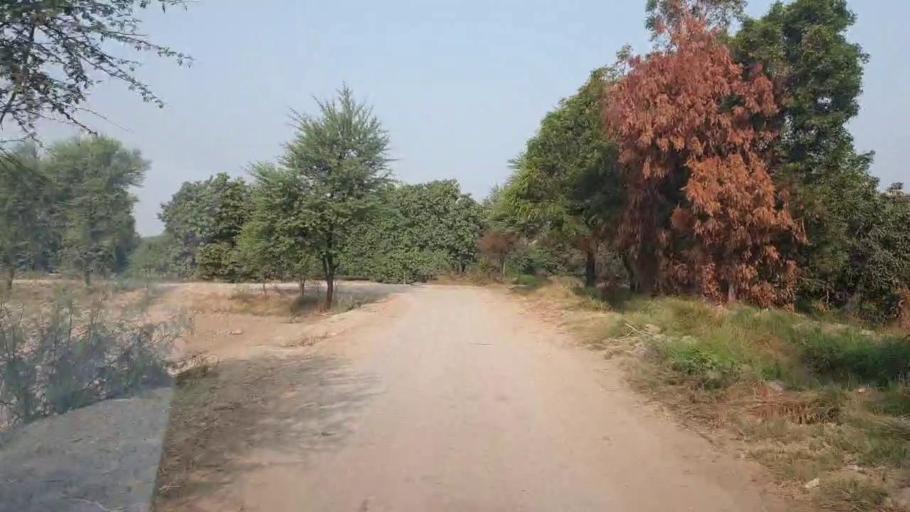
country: PK
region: Sindh
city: Tando Jam
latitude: 25.3345
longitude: 68.5323
